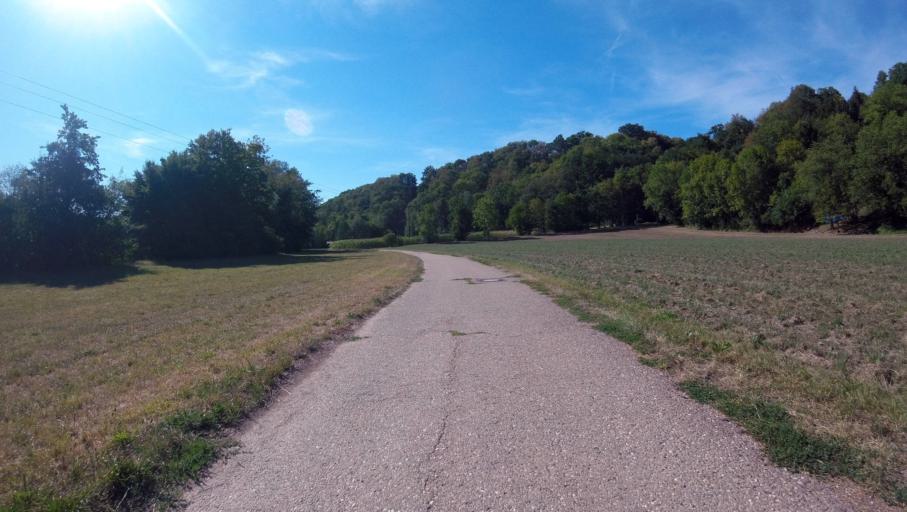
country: DE
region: Baden-Wuerttemberg
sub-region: Regierungsbezirk Stuttgart
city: Burgstetten
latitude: 48.9332
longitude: 9.3600
